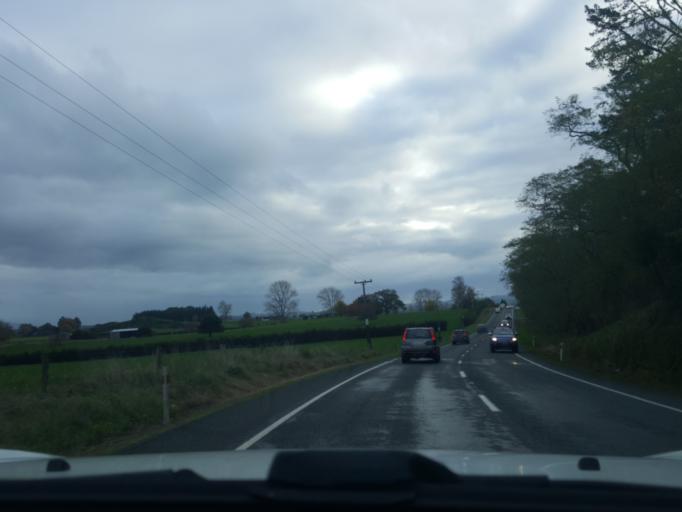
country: NZ
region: Waikato
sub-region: Matamata-Piako District
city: Matamata
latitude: -37.8903
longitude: 175.7860
